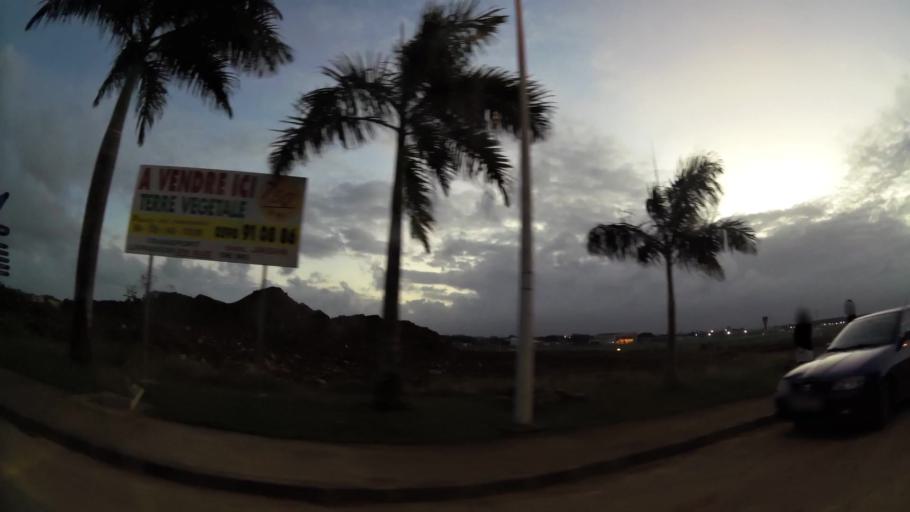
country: GP
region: Guadeloupe
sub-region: Guadeloupe
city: Les Abymes
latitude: 16.2655
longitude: -61.5160
